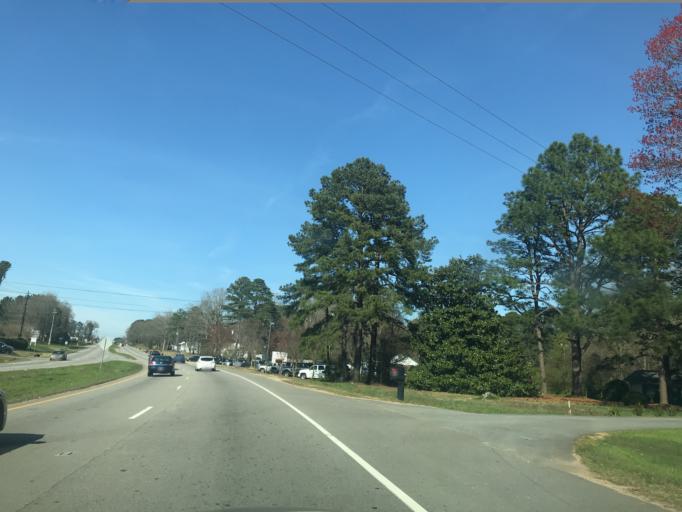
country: US
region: North Carolina
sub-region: Wake County
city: Garner
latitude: 35.7060
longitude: -78.6608
